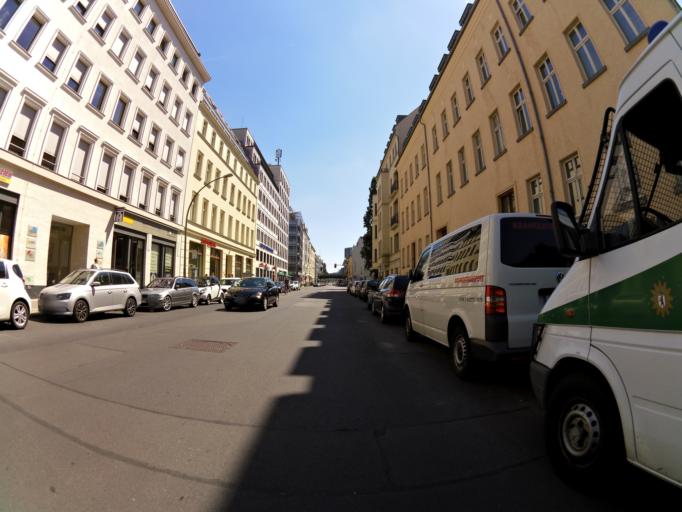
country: DE
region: Berlin
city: Tiergarten Bezirk
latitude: 52.5233
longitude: 13.3794
